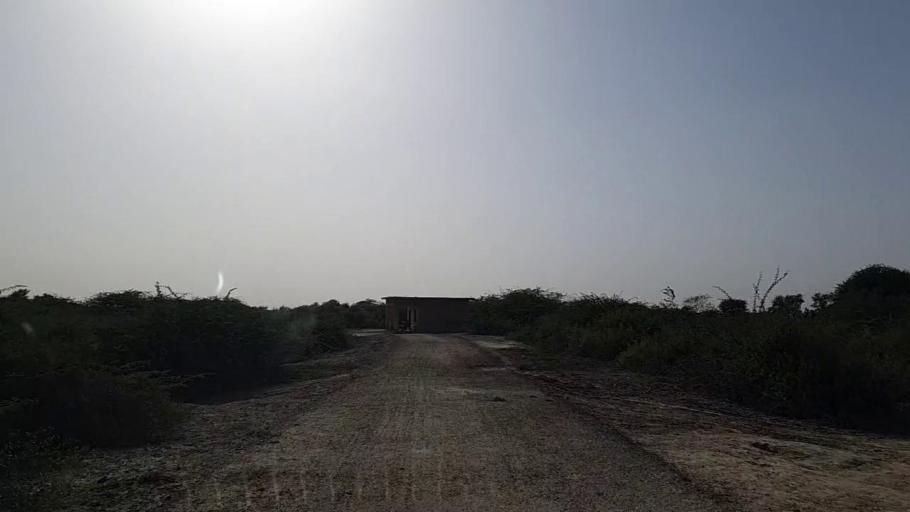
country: PK
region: Sindh
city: Jati
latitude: 24.2895
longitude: 68.2042
